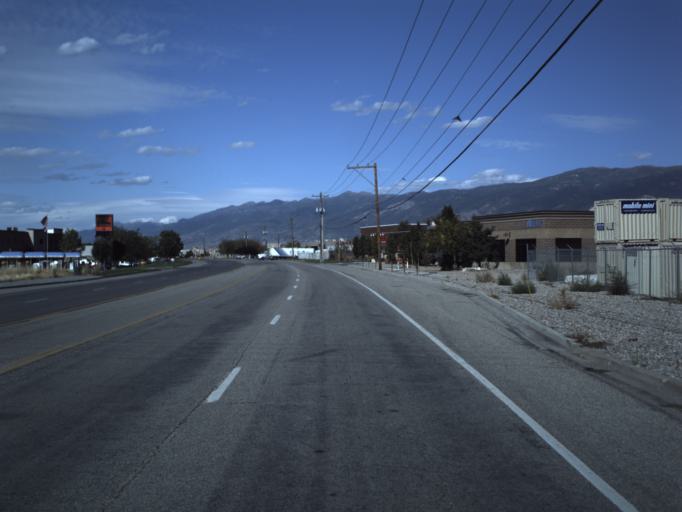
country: US
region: Utah
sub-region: Davis County
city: North Salt Lake
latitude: 40.8435
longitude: -111.9308
